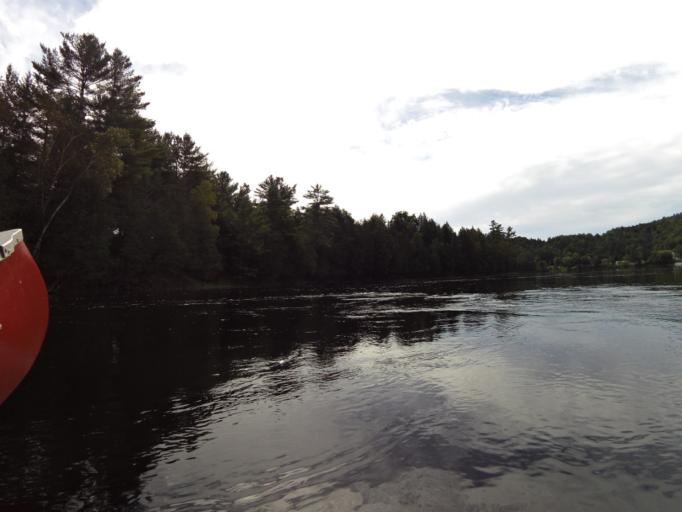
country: CA
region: Quebec
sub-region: Outaouais
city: Wakefield
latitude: 45.7764
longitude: -75.9399
